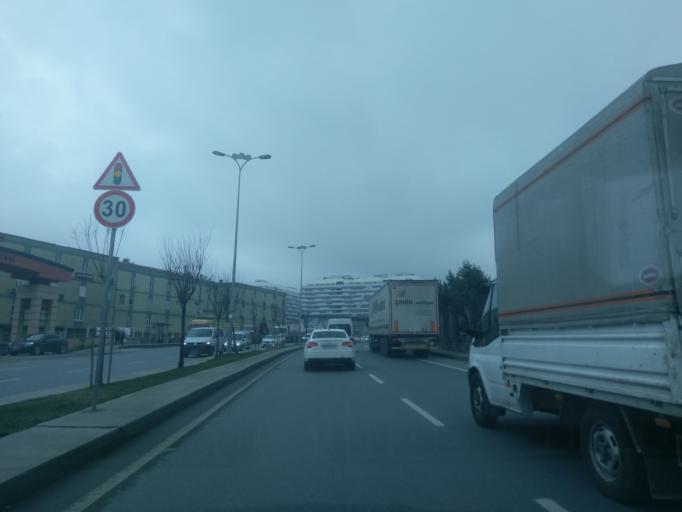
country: TR
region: Istanbul
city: Basaksehir
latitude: 41.0786
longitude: 28.7935
